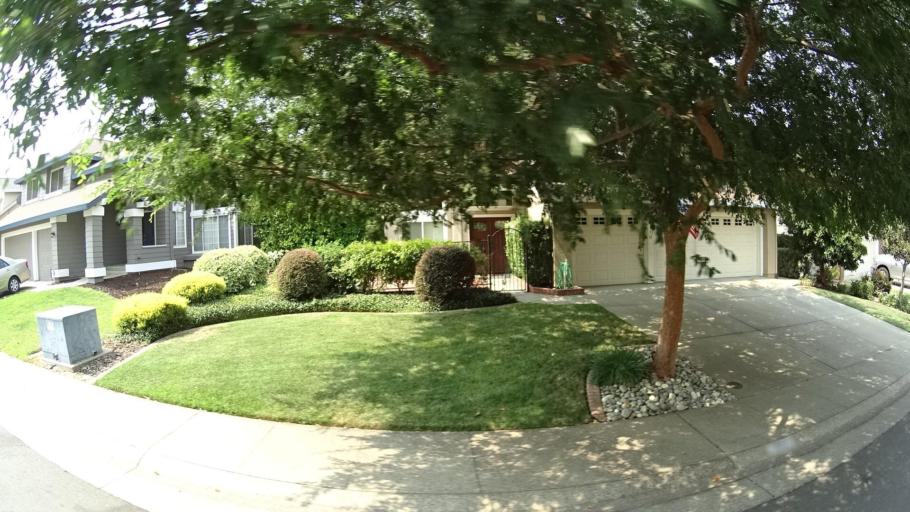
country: US
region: California
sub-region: Placer County
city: Rocklin
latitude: 38.8031
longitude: -121.2675
